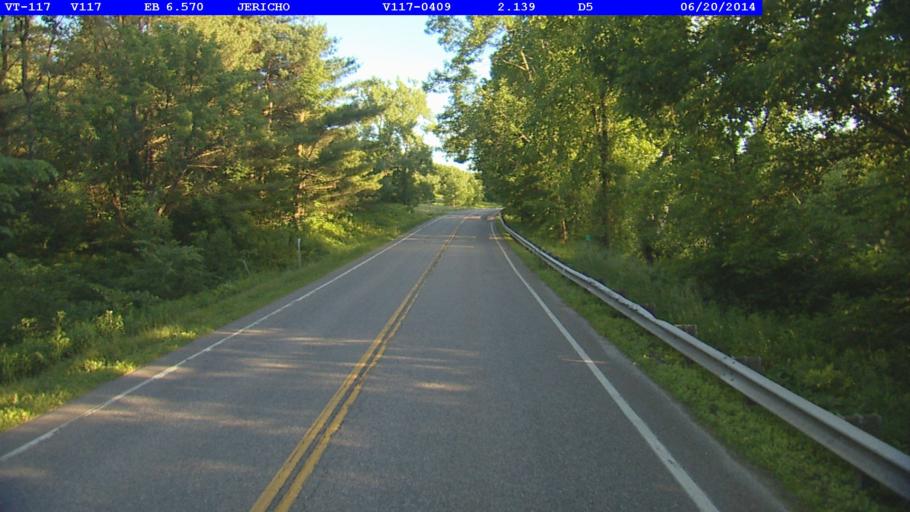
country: US
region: Vermont
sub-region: Chittenden County
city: Williston
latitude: 44.4447
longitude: -73.0190
